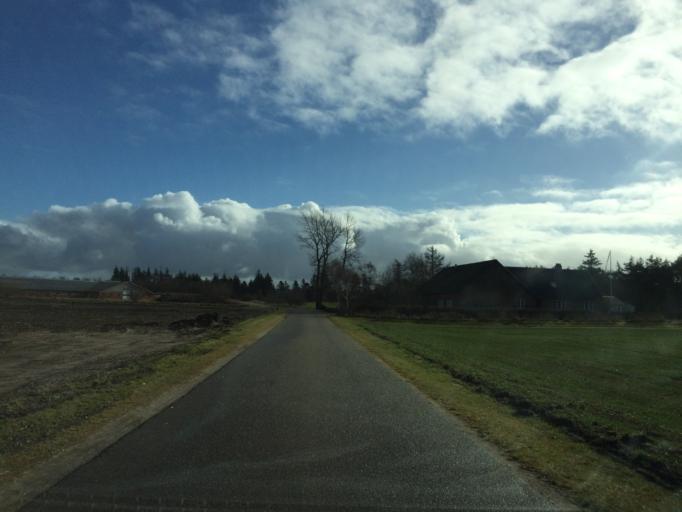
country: DK
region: Central Jutland
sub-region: Holstebro Kommune
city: Ulfborg
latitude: 56.2795
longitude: 8.3500
